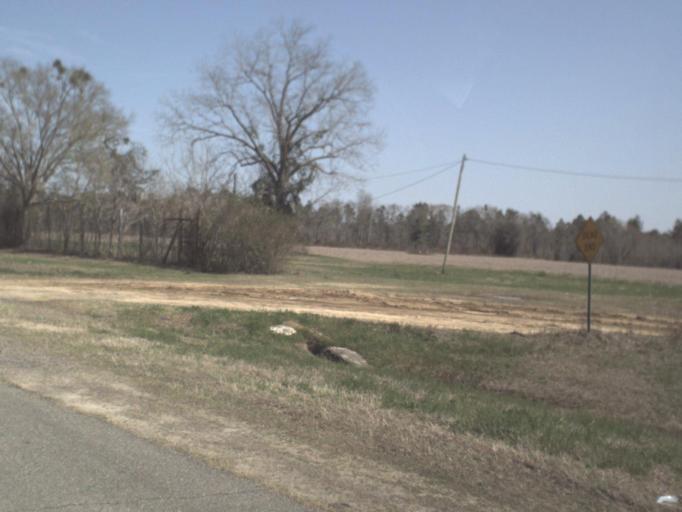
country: US
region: Florida
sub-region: Gadsden County
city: Gretna
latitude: 30.5748
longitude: -84.7027
